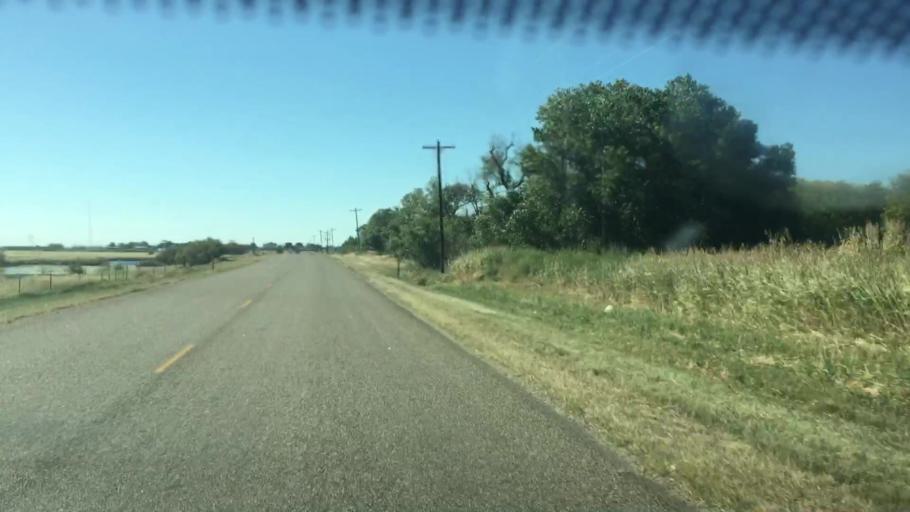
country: US
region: Colorado
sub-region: Prowers County
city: Lamar
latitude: 38.1162
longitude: -102.5955
